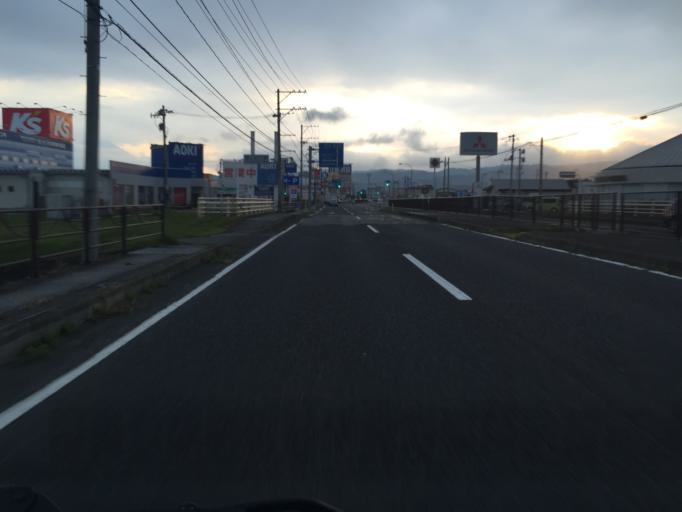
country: JP
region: Fukushima
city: Kitakata
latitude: 37.5174
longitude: 139.9132
